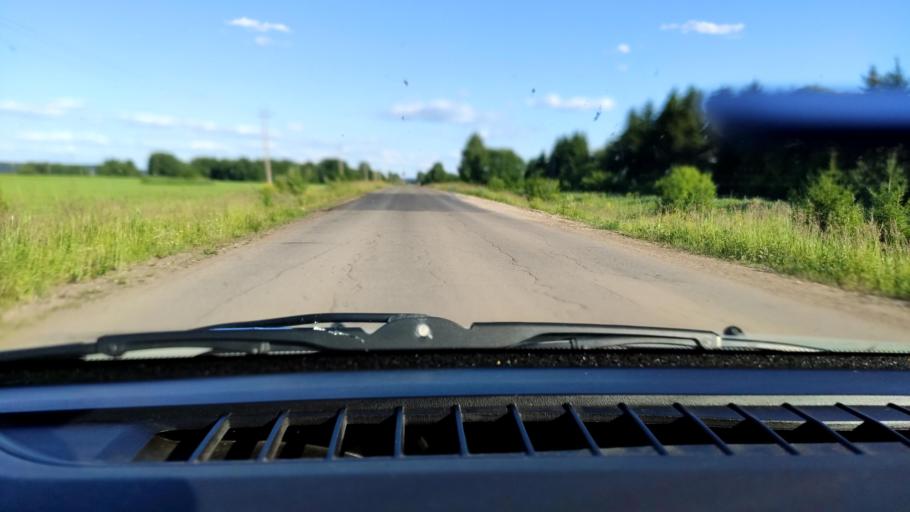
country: RU
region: Perm
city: Uinskoye
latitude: 57.1010
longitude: 56.5409
